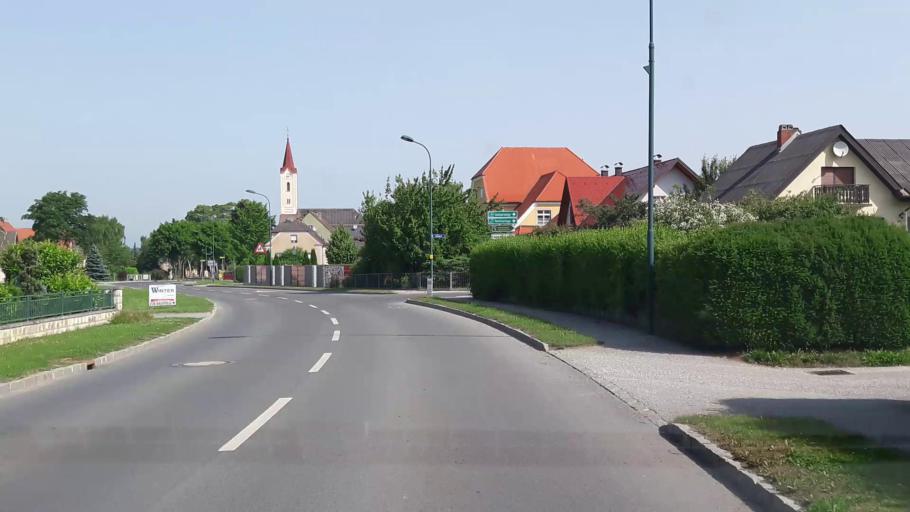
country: AT
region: Burgenland
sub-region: Politischer Bezirk Jennersdorf
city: Deutsch Kaltenbrunn
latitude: 47.0820
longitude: 16.1092
